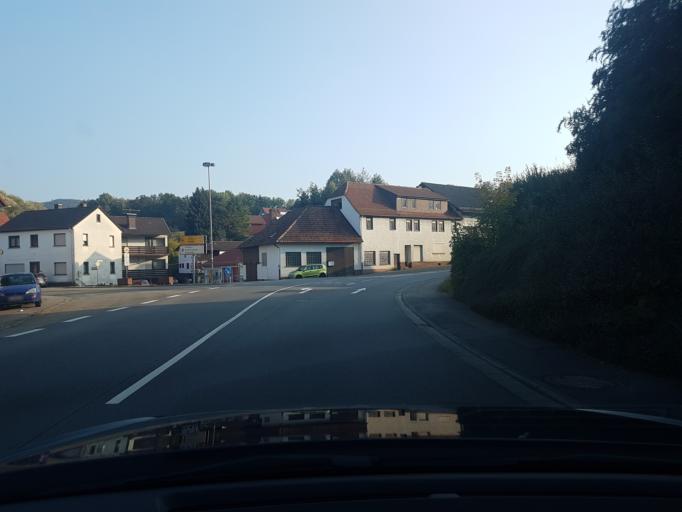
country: DE
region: Hesse
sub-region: Regierungsbezirk Darmstadt
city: Beerfelden
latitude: 49.5890
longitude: 8.9874
